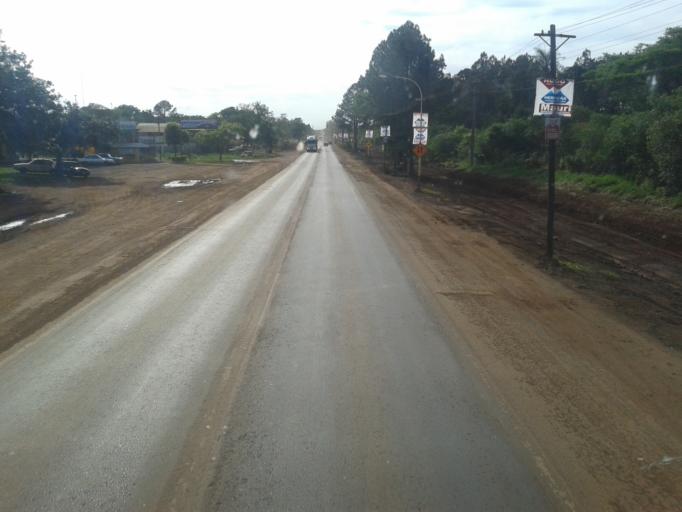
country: AR
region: Misiones
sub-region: Departamento de Candelaria
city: Candelaria
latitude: -27.4705
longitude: -55.7510
